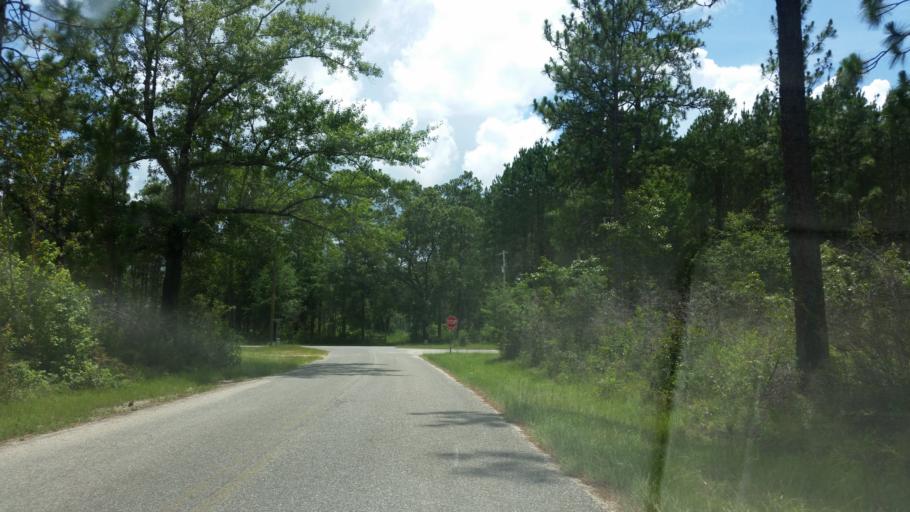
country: US
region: Florida
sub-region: Santa Rosa County
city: Point Baker
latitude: 30.7342
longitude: -86.8743
